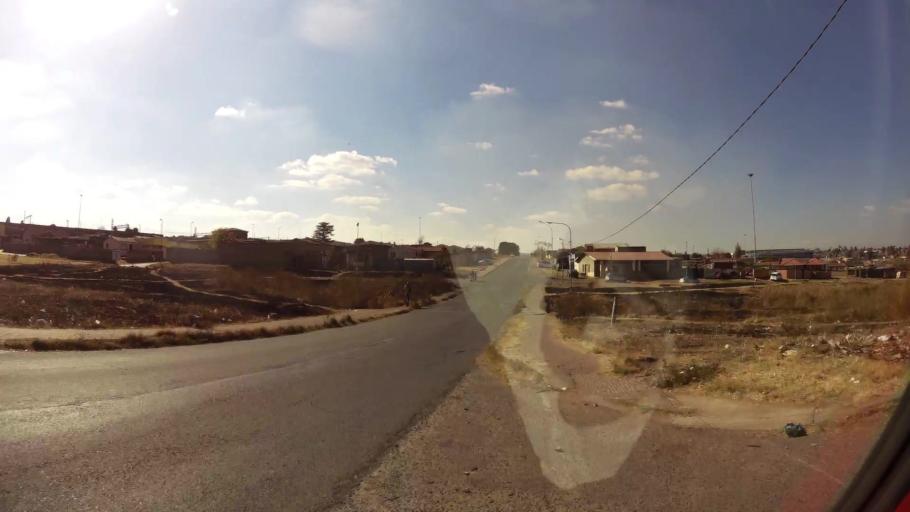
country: ZA
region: Gauteng
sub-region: City of Johannesburg Metropolitan Municipality
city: Soweto
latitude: -26.2272
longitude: 27.9133
